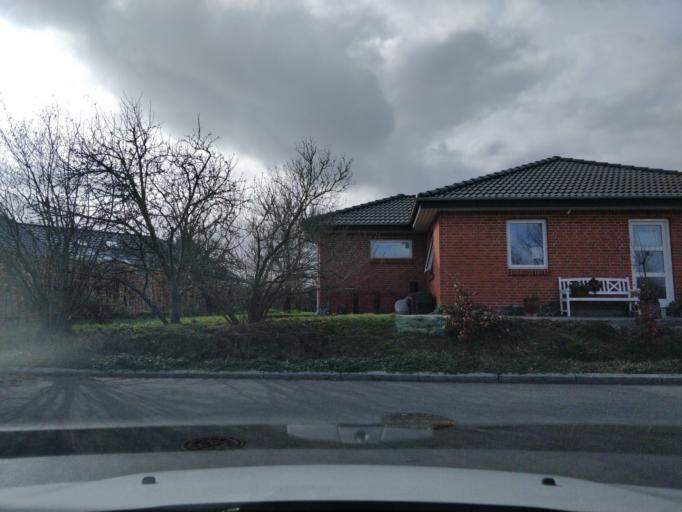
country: DK
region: Capital Region
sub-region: Hoje-Taastrup Kommune
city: Taastrup
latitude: 55.6496
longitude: 12.2521
